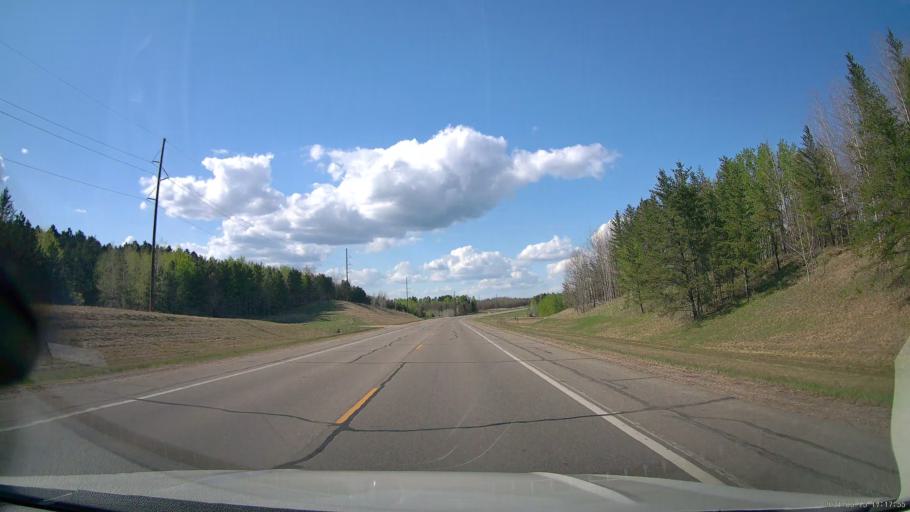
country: US
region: Minnesota
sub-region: Hubbard County
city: Park Rapids
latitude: 46.9528
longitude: -95.0179
